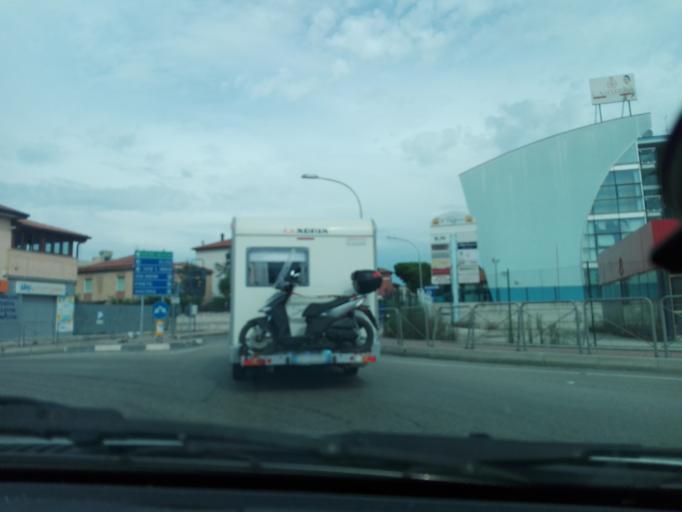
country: IT
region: Abruzzo
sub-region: Provincia di Pescara
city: Montesilvano Marina
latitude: 42.5231
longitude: 14.1422
